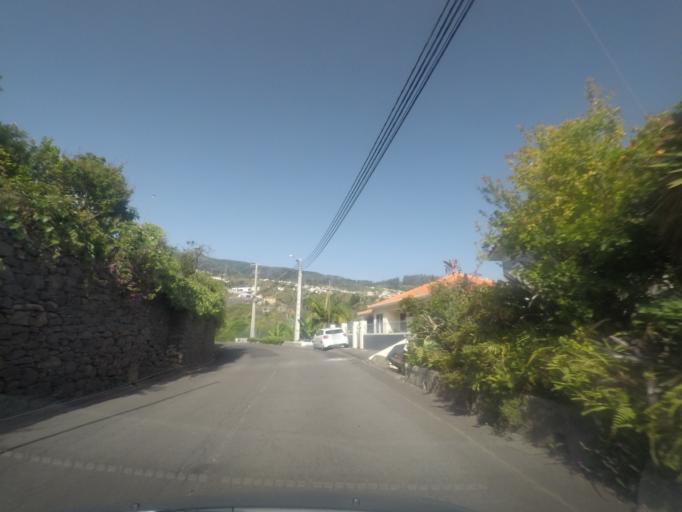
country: PT
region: Madeira
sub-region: Calheta
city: Estreito da Calheta
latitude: 32.7293
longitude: -17.1708
